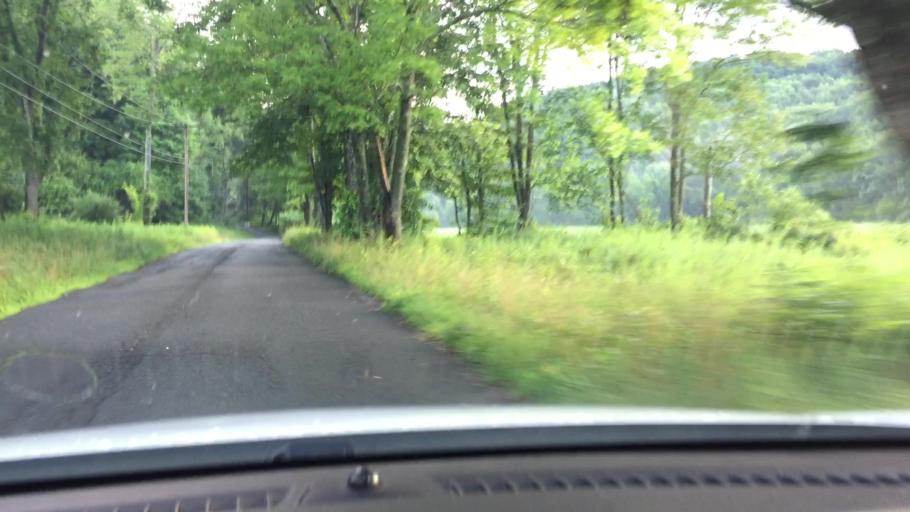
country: US
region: Massachusetts
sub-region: Hampshire County
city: Chesterfield
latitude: 42.3282
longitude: -72.9328
